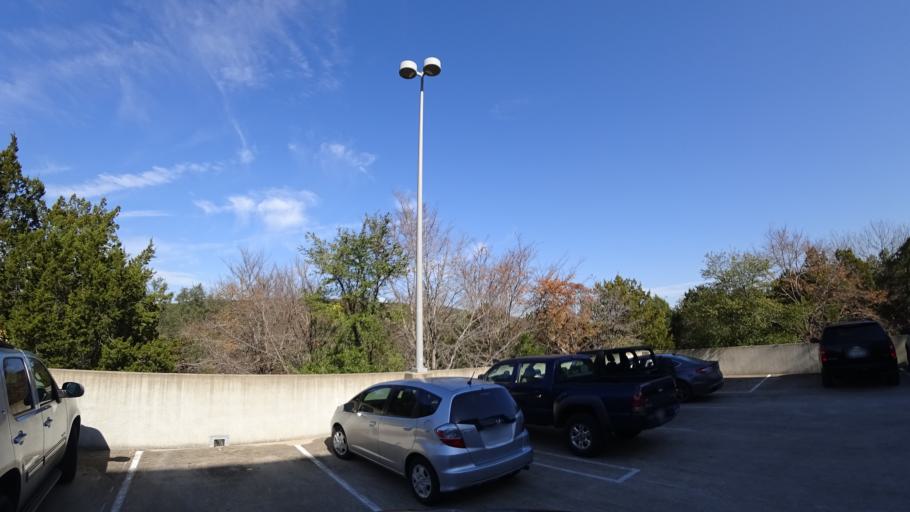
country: US
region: Texas
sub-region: Williamson County
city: Jollyville
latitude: 30.3769
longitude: -97.7779
